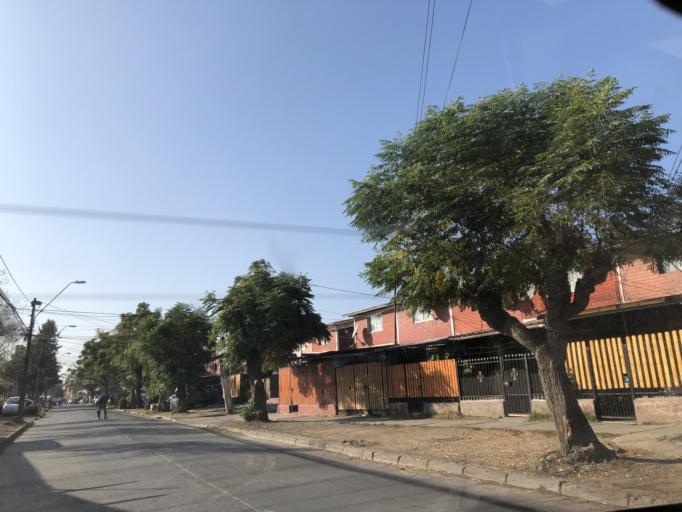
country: CL
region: Santiago Metropolitan
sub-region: Provincia de Cordillera
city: Puente Alto
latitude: -33.6244
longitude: -70.5958
